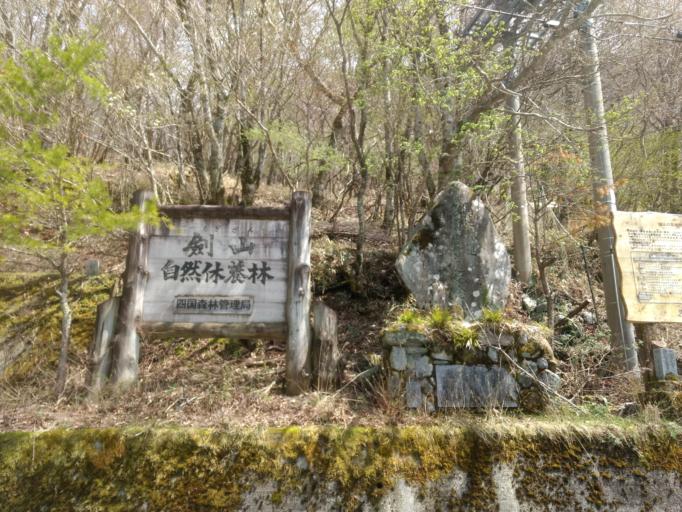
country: JP
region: Tokushima
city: Wakimachi
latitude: 33.8673
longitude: 134.0897
